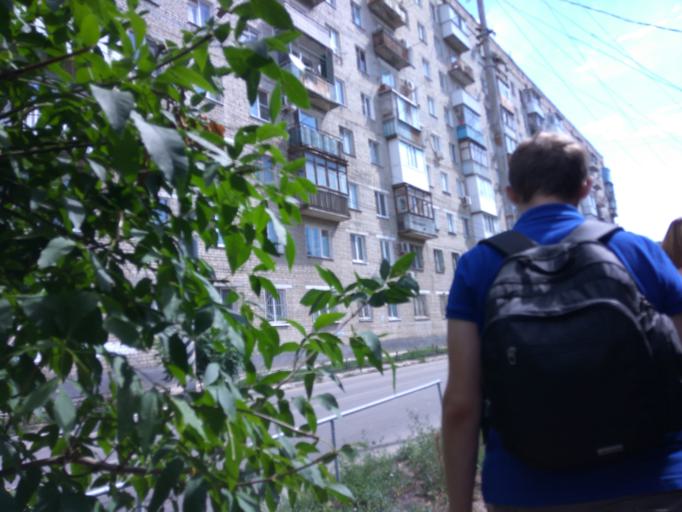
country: RU
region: Saratov
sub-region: Saratovskiy Rayon
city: Saratov
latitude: 51.5320
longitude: 46.0501
